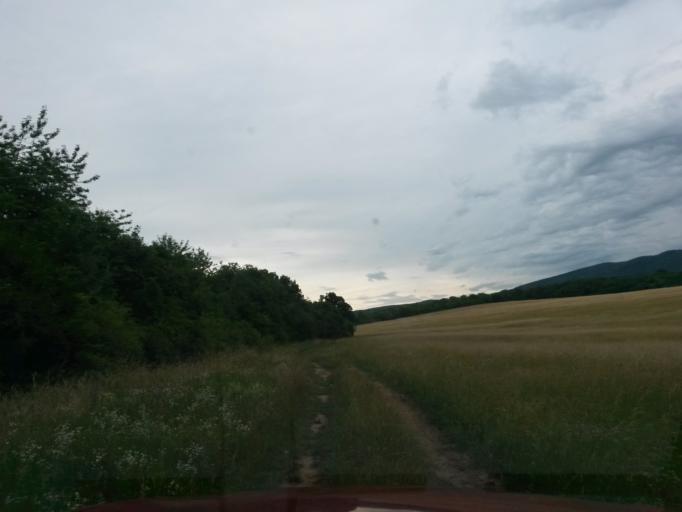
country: SK
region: Banskobystricky
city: Velky Krtis
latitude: 48.3153
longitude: 19.4196
